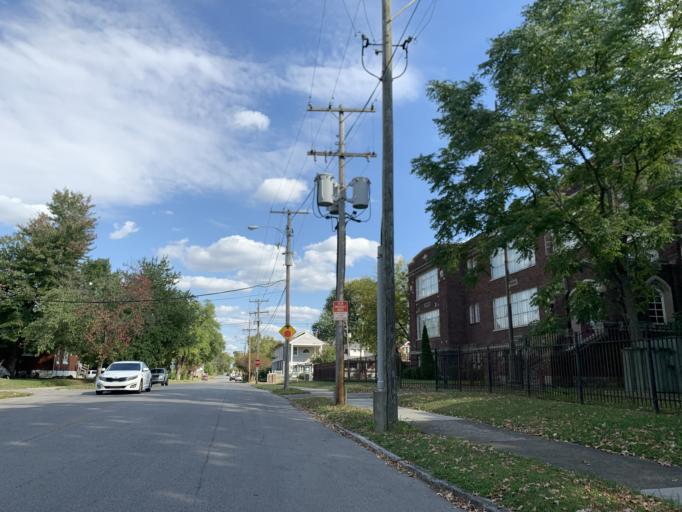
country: US
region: Indiana
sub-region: Floyd County
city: New Albany
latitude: 38.2467
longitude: -85.8192
